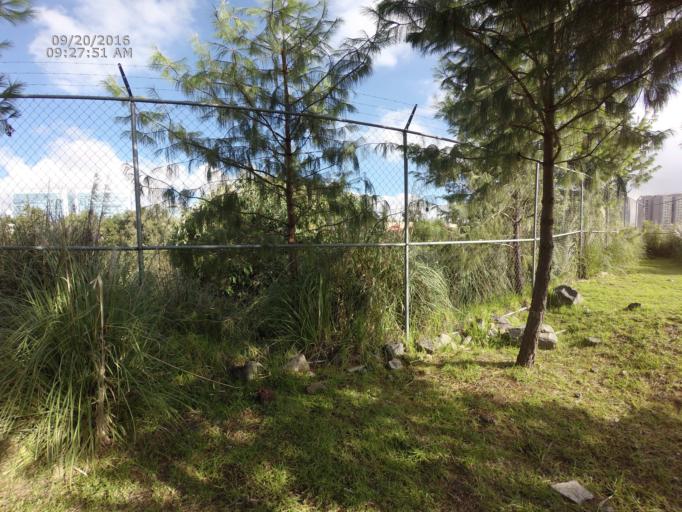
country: MX
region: Mexico City
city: Col. Bosques de las Lomas
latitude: 19.3623
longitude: -99.2553
